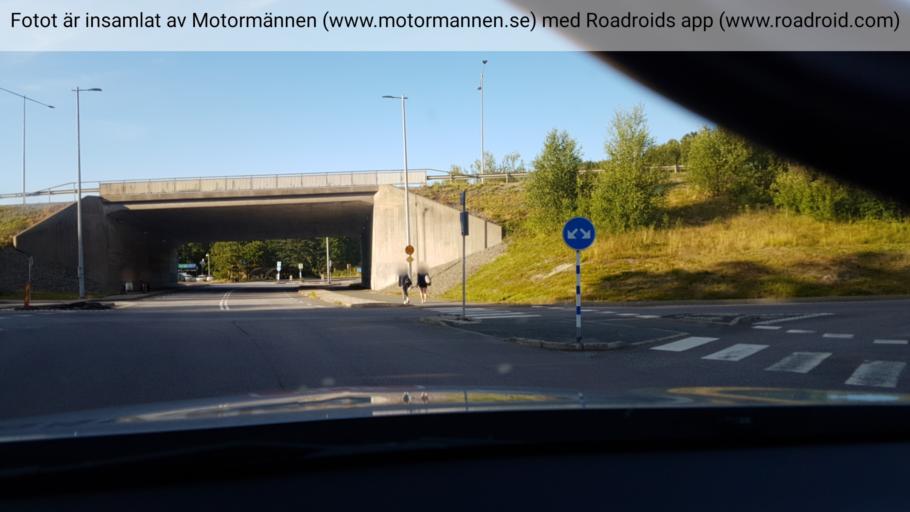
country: SE
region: Vaestra Goetaland
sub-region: Molndal
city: Moelndal
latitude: 57.6755
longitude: 12.0262
